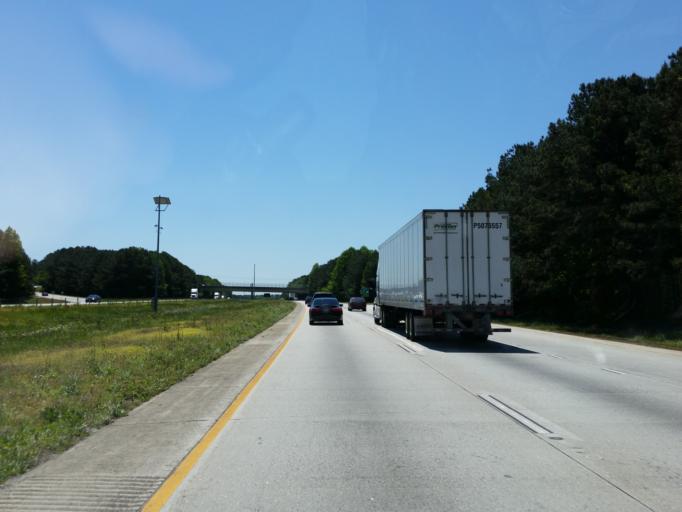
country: US
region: Georgia
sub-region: Clayton County
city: Morrow
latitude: 33.5819
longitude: -84.2800
